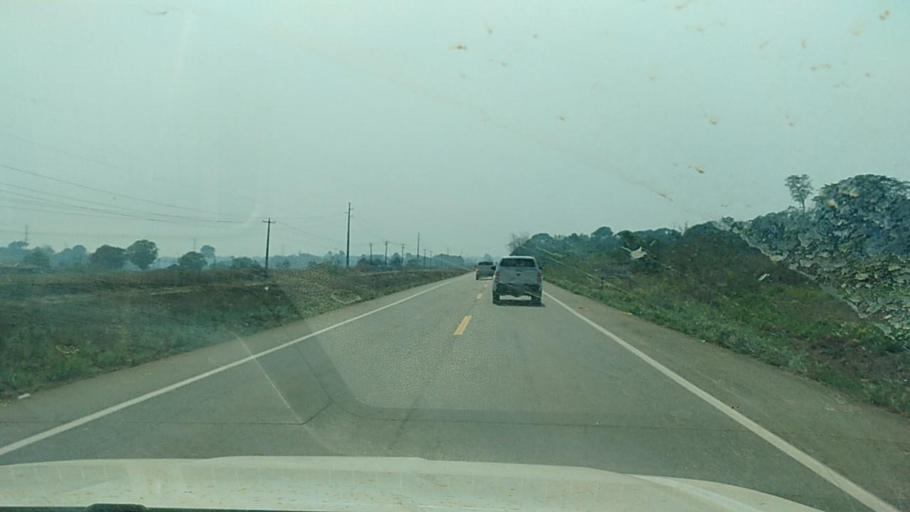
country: BR
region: Rondonia
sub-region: Porto Velho
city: Porto Velho
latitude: -8.7812
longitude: -63.5486
